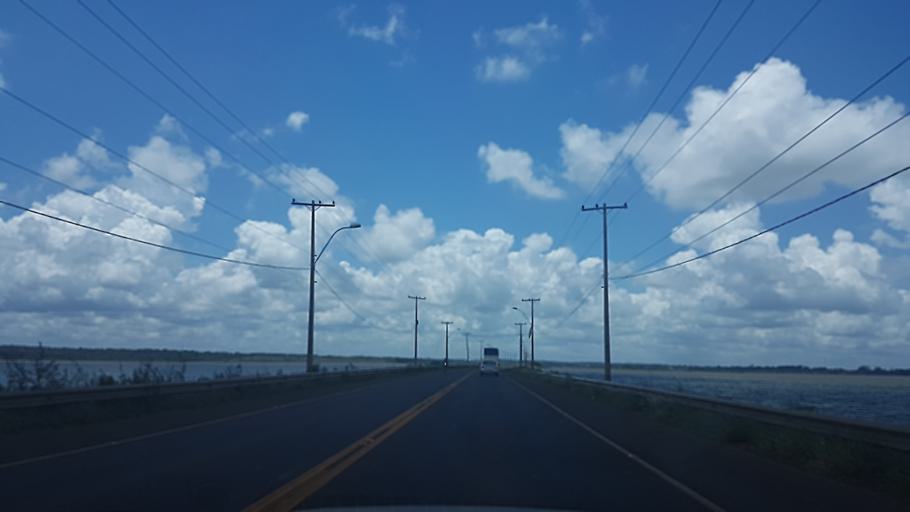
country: PY
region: Itapua
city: Carmen del Parana
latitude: -27.2014
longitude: -56.1776
